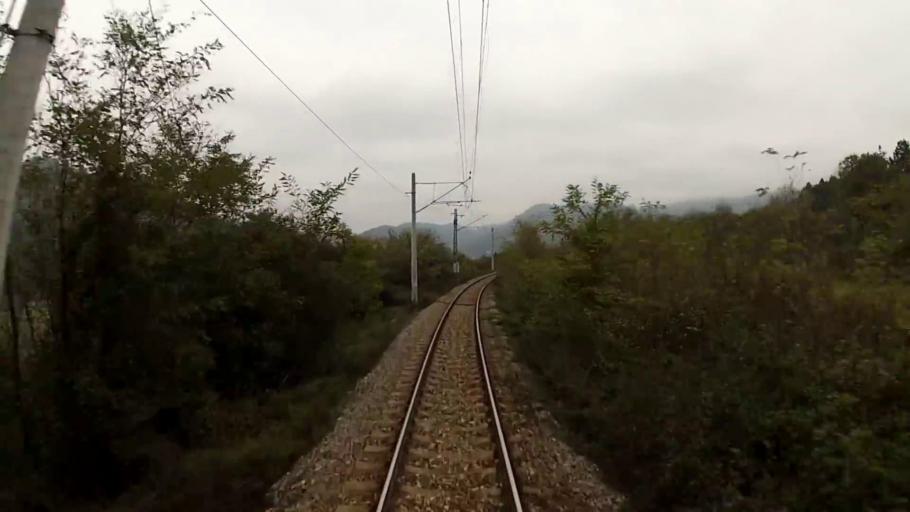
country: RS
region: Central Serbia
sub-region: Pirotski Okrug
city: Dimitrovgrad
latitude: 42.9880
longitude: 22.8515
